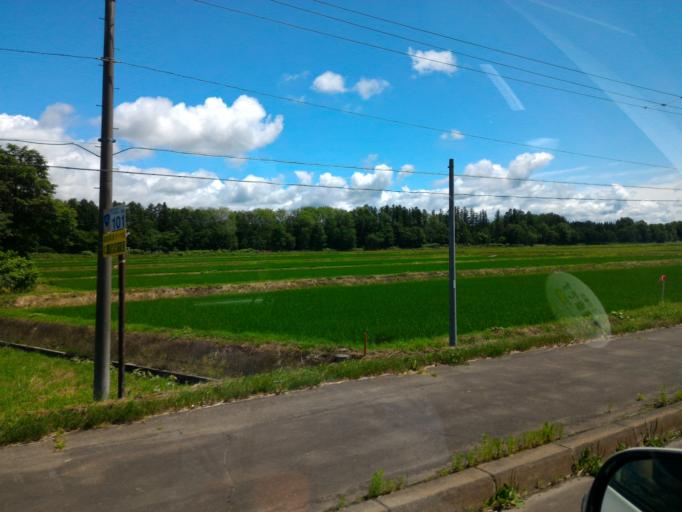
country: JP
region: Hokkaido
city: Nayoro
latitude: 44.5102
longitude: 142.3327
